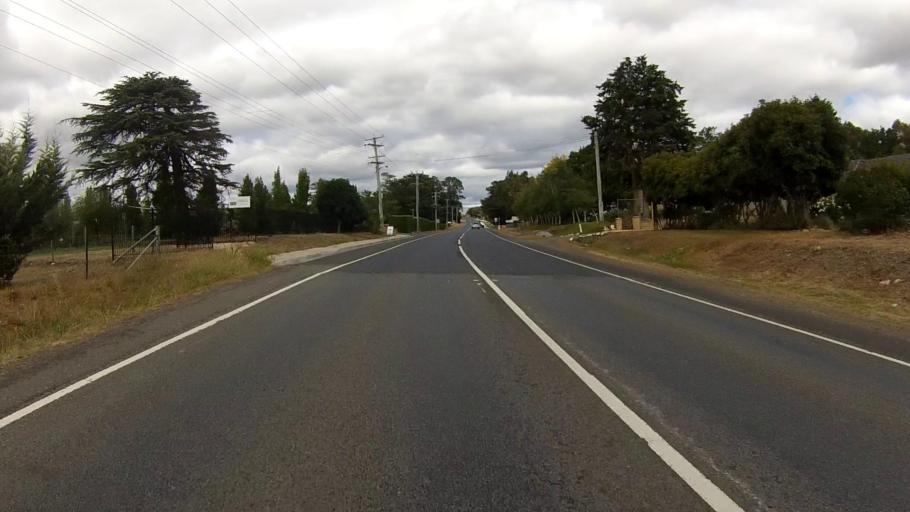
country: AU
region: Tasmania
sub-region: Brighton
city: Bridgewater
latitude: -42.6860
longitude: 147.2654
